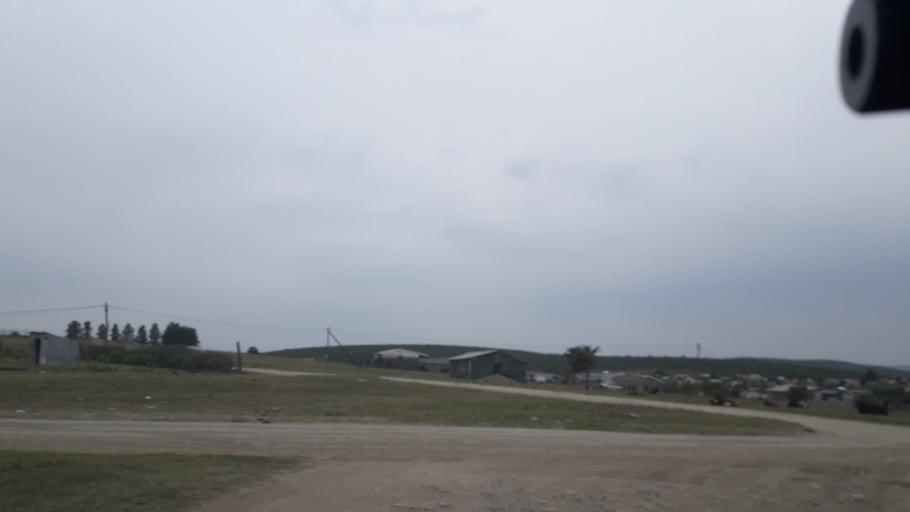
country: ZA
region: Eastern Cape
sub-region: Buffalo City Metropolitan Municipality
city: Bhisho
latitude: -32.7957
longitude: 27.3452
